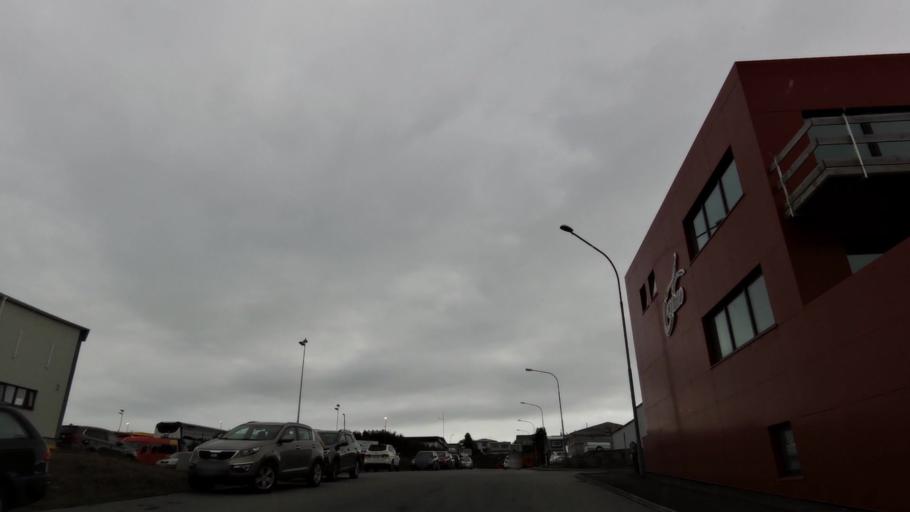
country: IS
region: Capital Region
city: Hafnarfjoerdur
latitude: 64.0597
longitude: -21.9763
